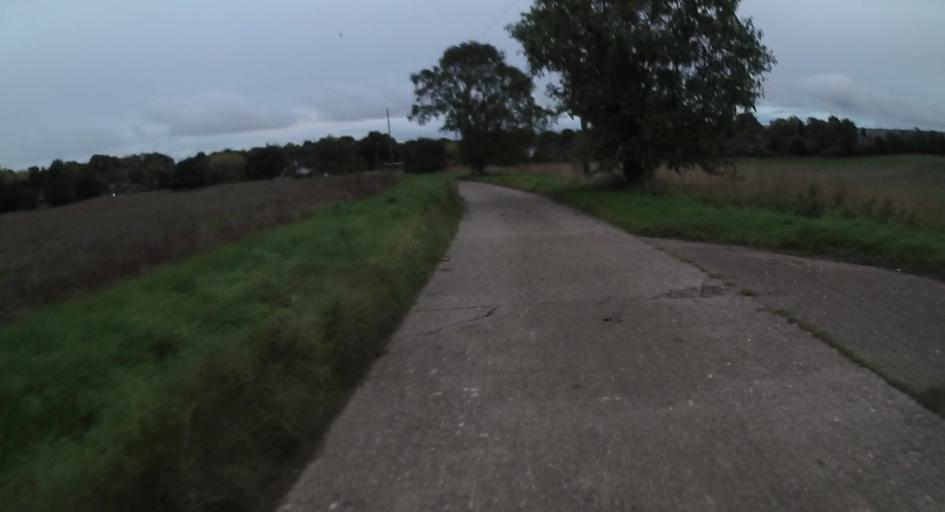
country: GB
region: England
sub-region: Hampshire
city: Basingstoke
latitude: 51.2699
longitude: -1.1326
